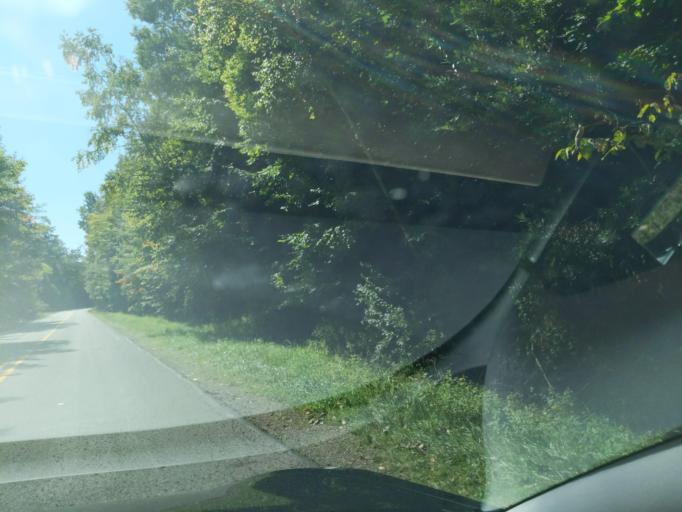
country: US
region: Michigan
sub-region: Antrim County
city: Elk Rapids
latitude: 44.9526
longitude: -85.3224
